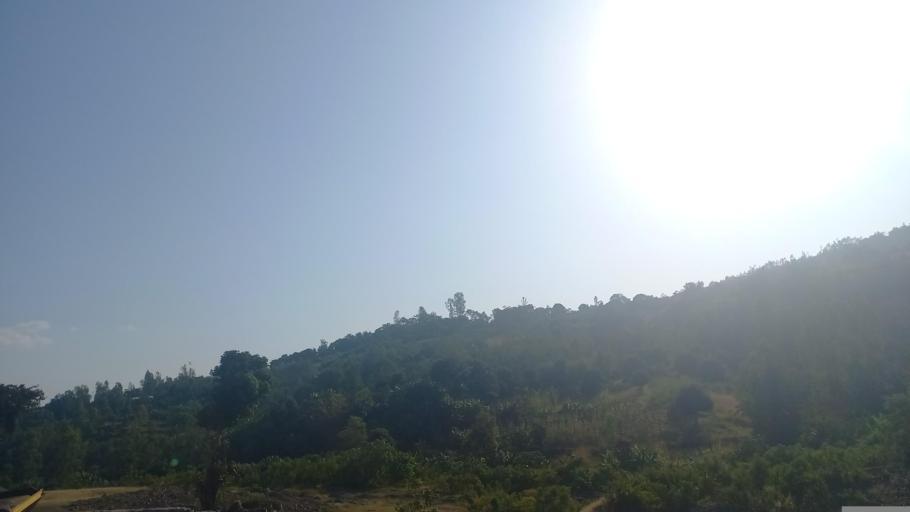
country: ET
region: Southern Nations, Nationalities, and People's Region
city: Areka
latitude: 7.2290
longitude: 37.5928
